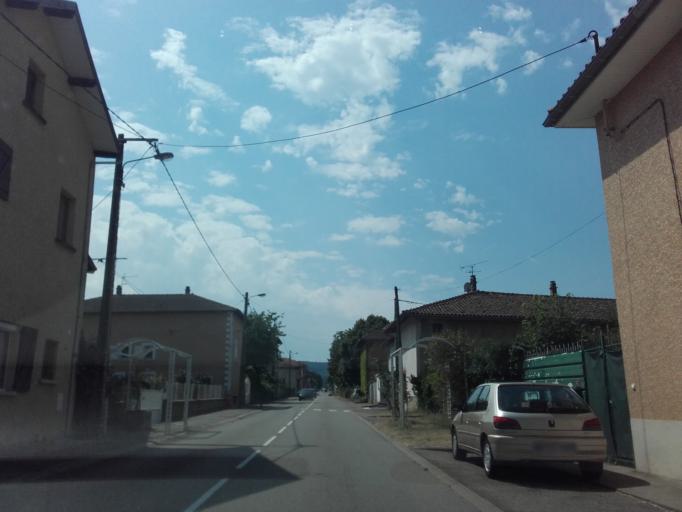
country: FR
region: Rhone-Alpes
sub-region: Departement de l'Isere
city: Saint-Simeon-de-Bressieux
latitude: 45.3320
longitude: 5.2664
